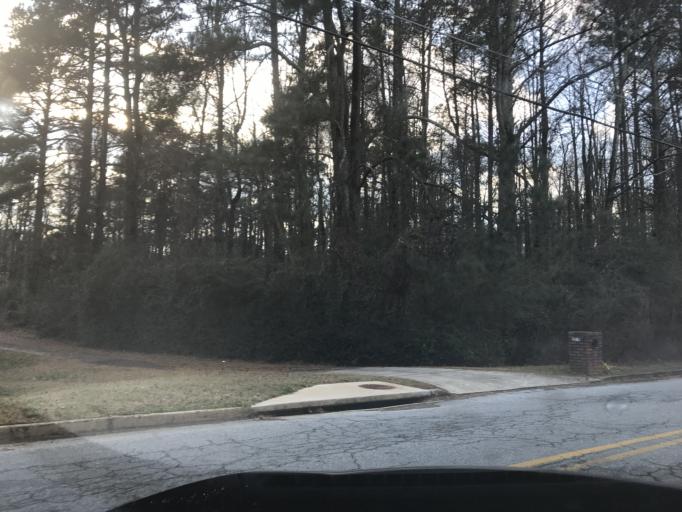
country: US
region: Georgia
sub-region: Fulton County
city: College Park
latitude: 33.6385
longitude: -84.4790
